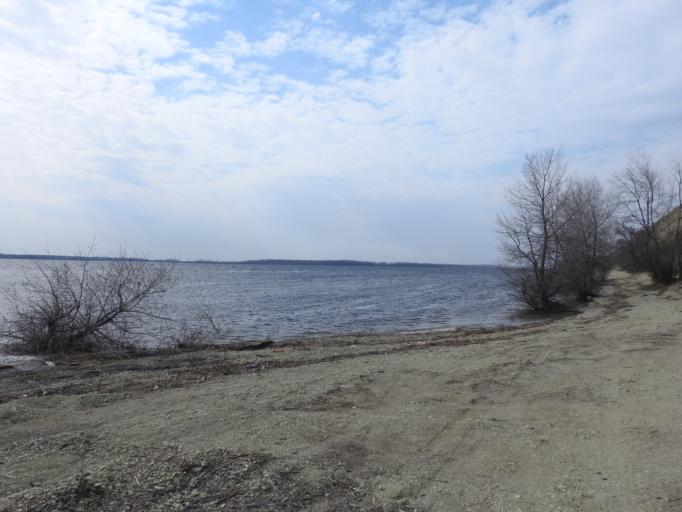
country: RU
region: Saratov
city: Voskresenskoye
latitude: 51.8081
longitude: 46.9207
